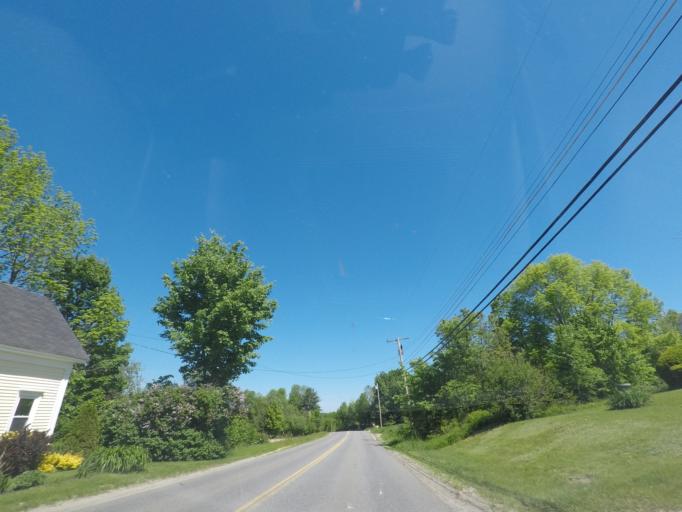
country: US
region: Maine
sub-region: Kennebec County
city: Manchester
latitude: 44.2401
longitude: -69.8910
